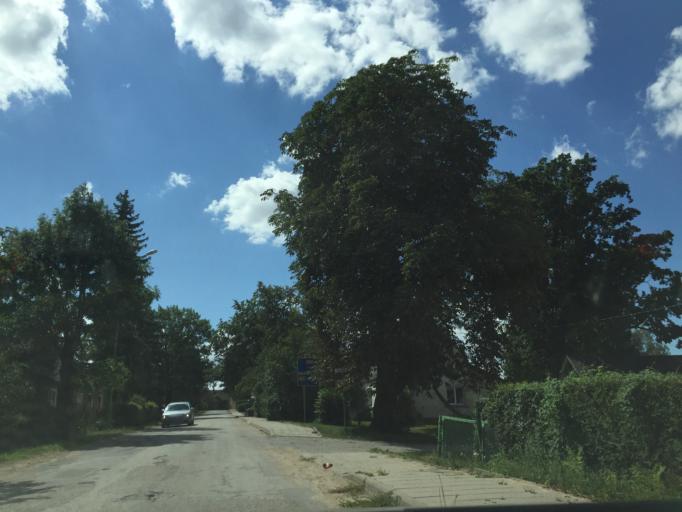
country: LV
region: Rundales
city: Pilsrundale
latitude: 56.2749
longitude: 24.0003
